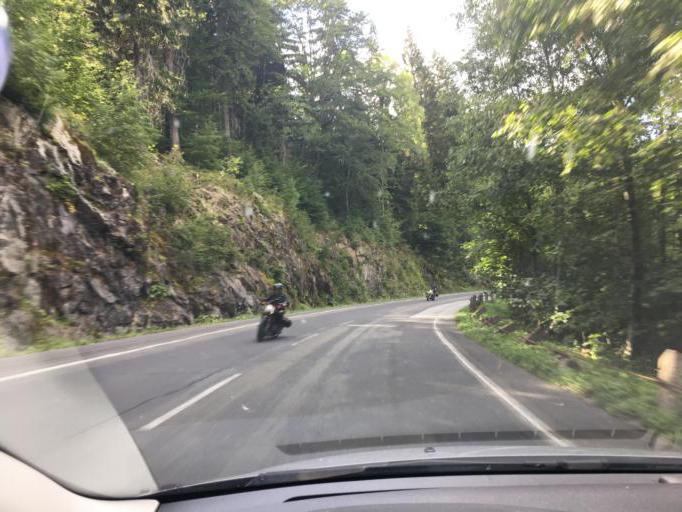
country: CZ
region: Kralovehradecky
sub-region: Okres Trutnov
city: Spindleruv Mlyn
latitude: 50.7014
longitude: 15.5843
